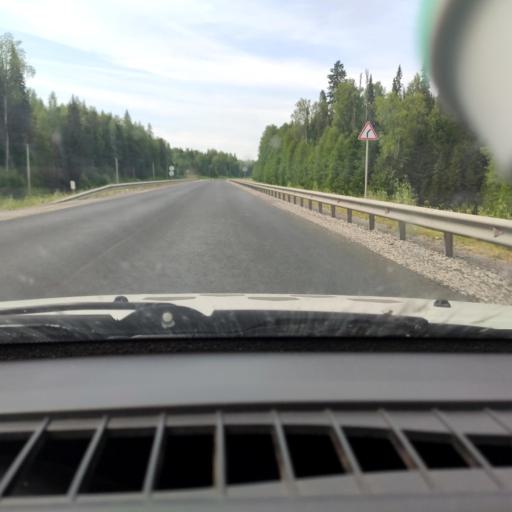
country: RU
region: Perm
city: Siva
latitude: 58.5523
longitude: 53.9027
